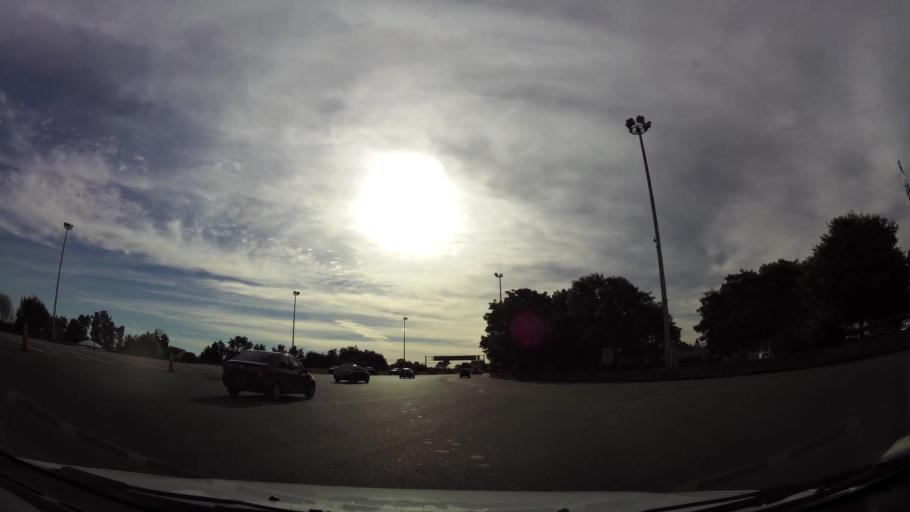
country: AR
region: Buenos Aires F.D.
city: Villa Lugano
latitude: -34.6475
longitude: -58.4793
